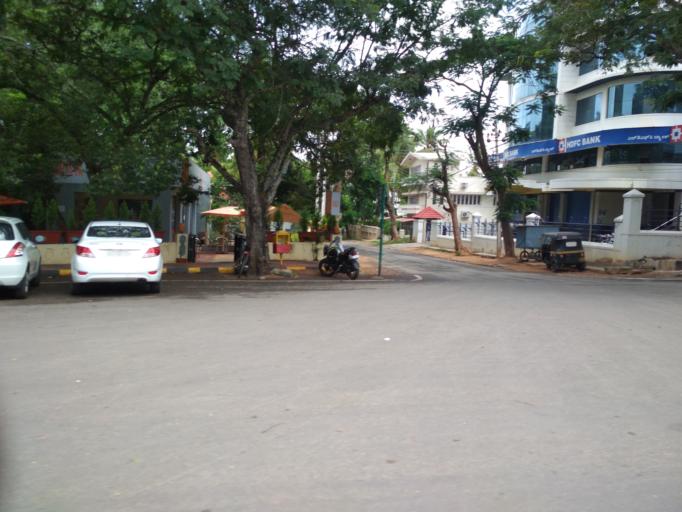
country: IN
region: Karnataka
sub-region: Mysore
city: Mysore
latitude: 12.3245
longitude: 76.6315
